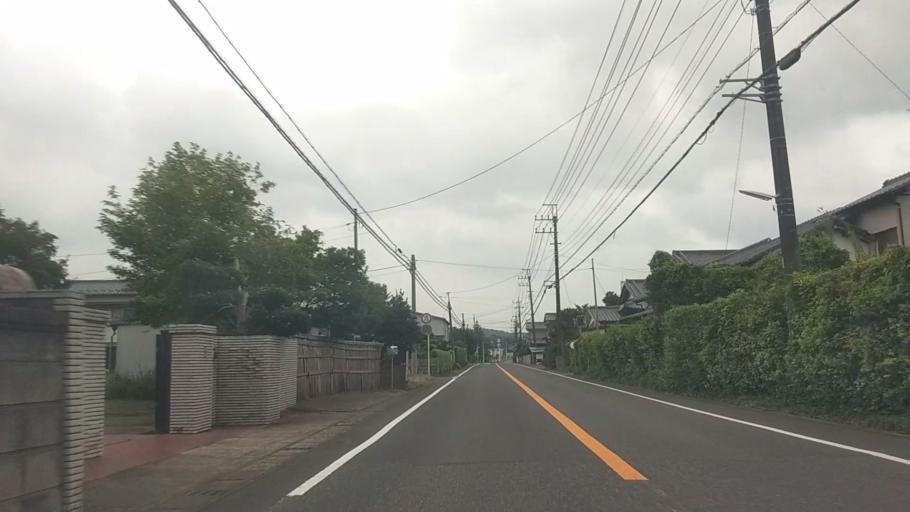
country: JP
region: Chiba
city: Ichihara
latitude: 35.3892
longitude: 140.0529
